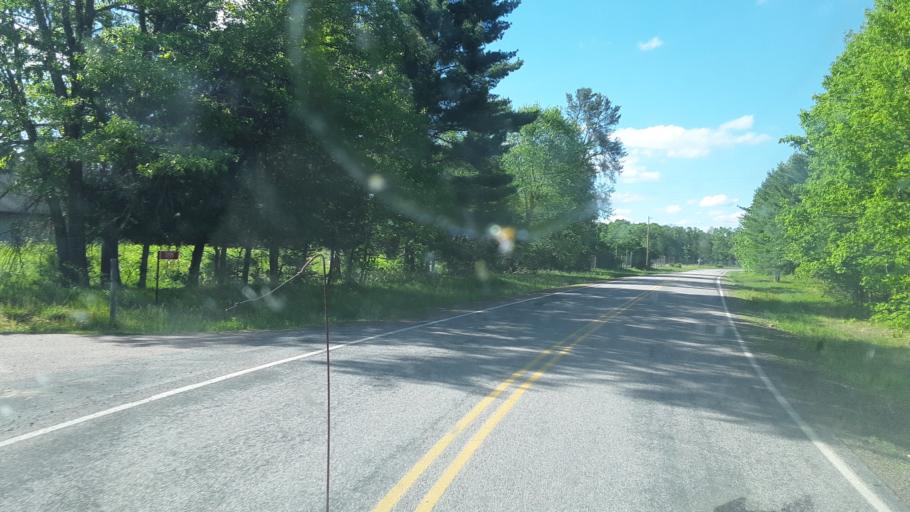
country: US
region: Wisconsin
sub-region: Wood County
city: Nekoosa
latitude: 44.3071
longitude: -90.1296
